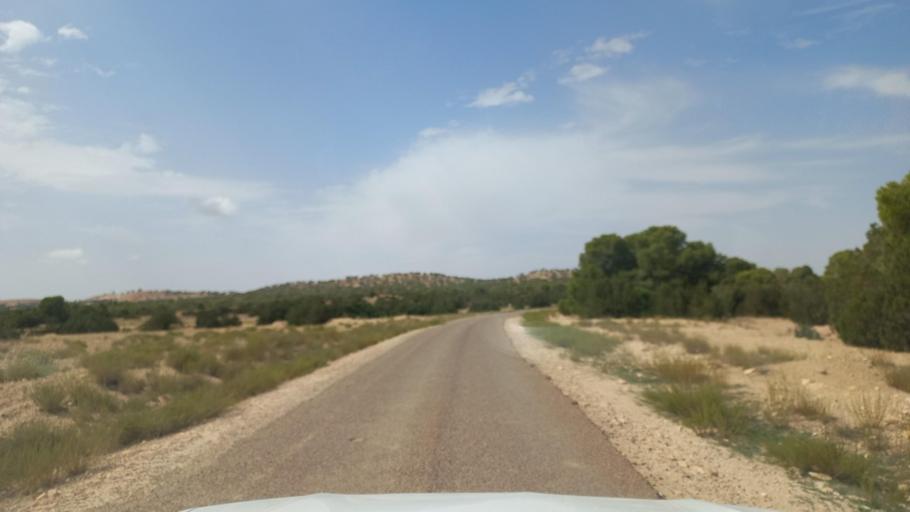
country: TN
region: Al Qasrayn
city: Sbiba
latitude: 35.4107
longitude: 8.9284
